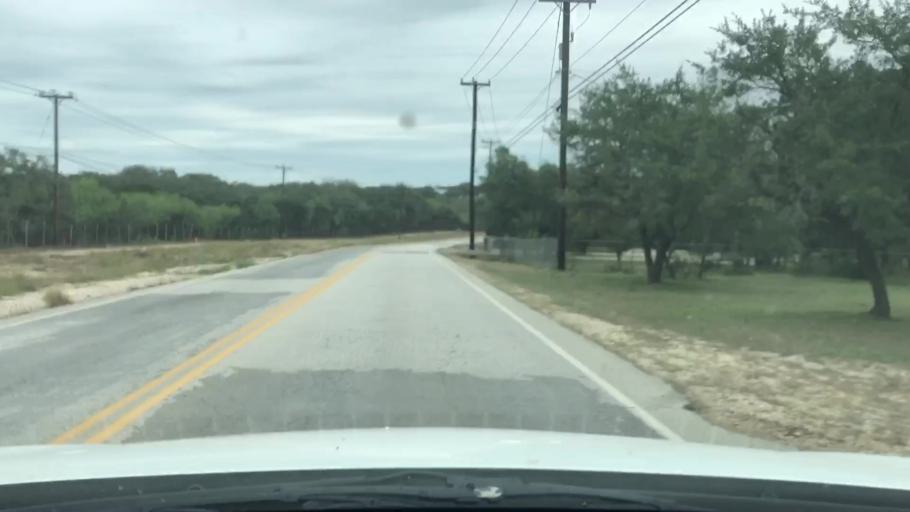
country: US
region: Texas
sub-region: Bexar County
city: Timberwood Park
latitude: 29.6485
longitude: -98.4175
